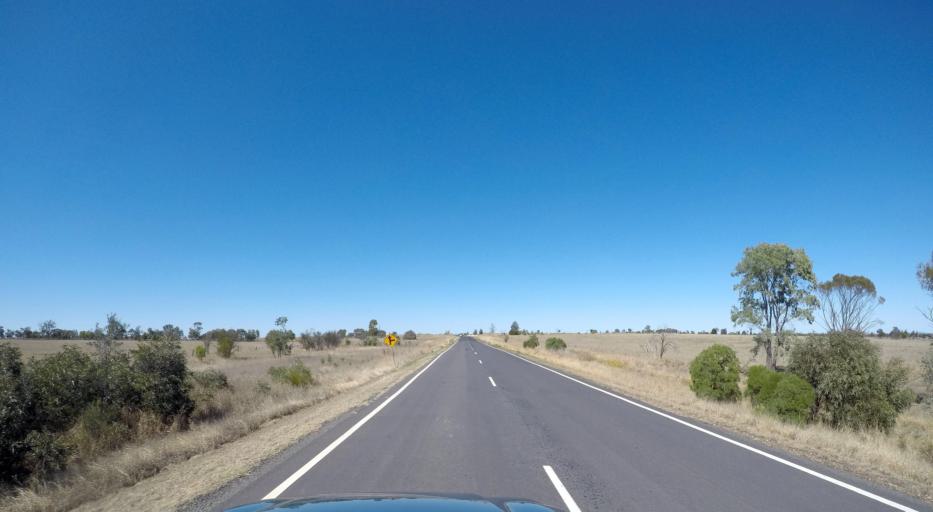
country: AU
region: Queensland
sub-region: Banana
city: Taroom
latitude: -26.0157
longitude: 149.9112
